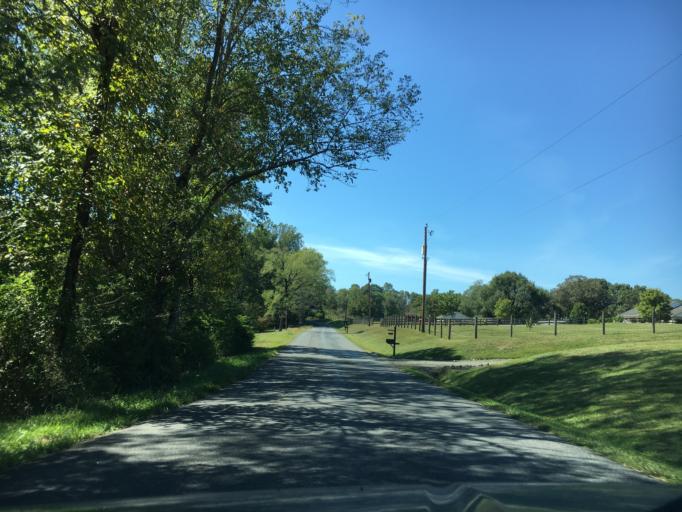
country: US
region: Virginia
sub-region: Albemarle County
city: Crozet
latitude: 38.0172
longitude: -78.7586
